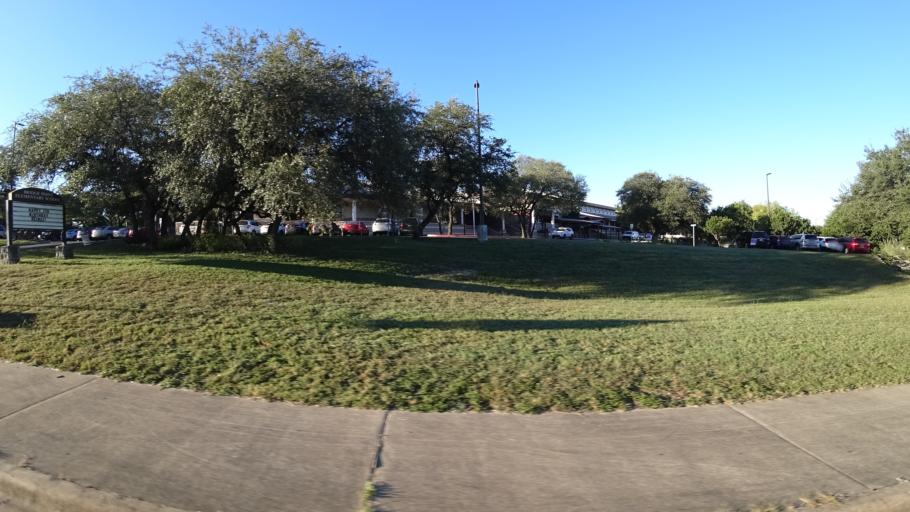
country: US
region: Texas
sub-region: Travis County
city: West Lake Hills
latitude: 30.3403
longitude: -97.8053
